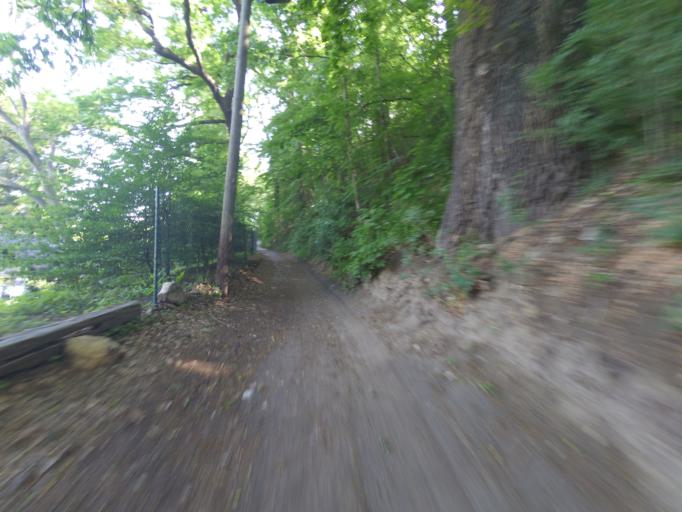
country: DE
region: Thuringia
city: Rudolstadt
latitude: 50.7071
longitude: 11.3295
